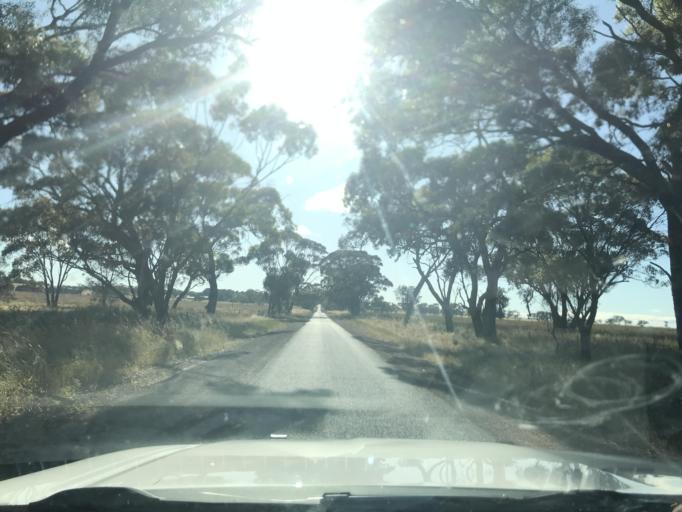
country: AU
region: Victoria
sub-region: Horsham
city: Horsham
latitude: -36.6985
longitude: 141.6099
